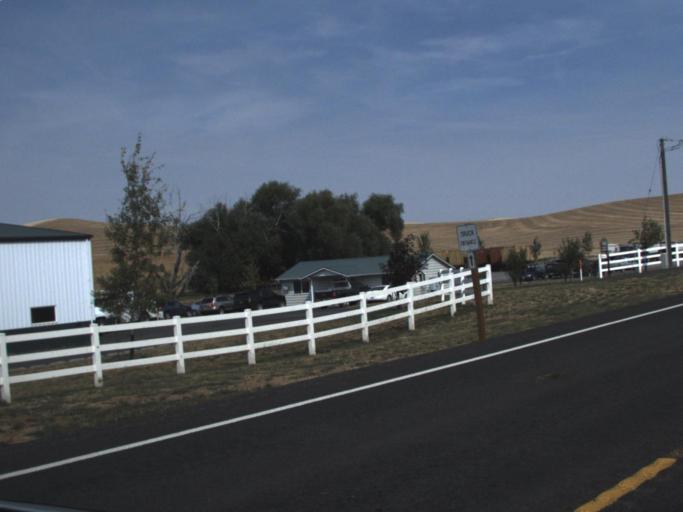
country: US
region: Washington
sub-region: Whitman County
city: Pullman
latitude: 46.7691
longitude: -117.1650
